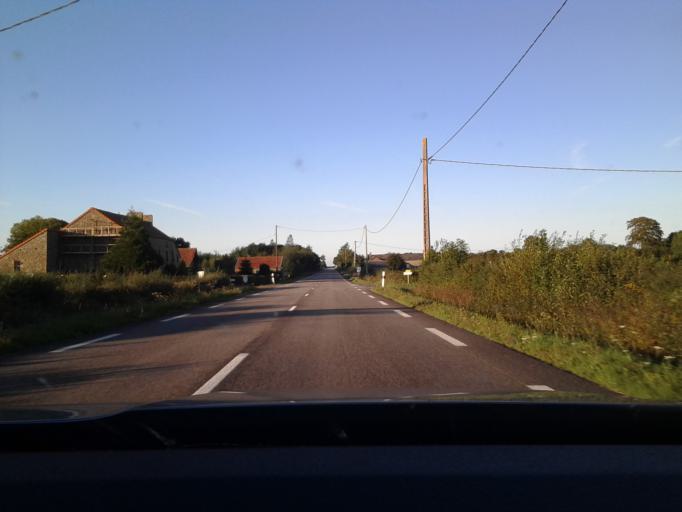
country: FR
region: Lower Normandy
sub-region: Departement de la Manche
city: Saint-Sauveur-le-Vicomte
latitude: 49.4090
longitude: -1.5073
